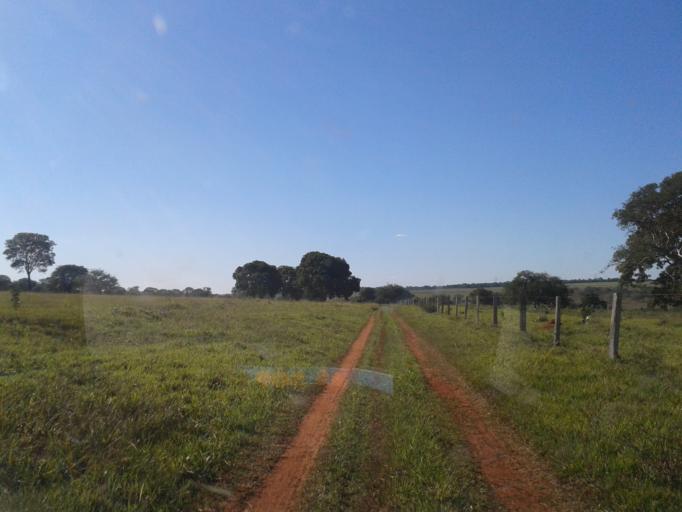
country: BR
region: Minas Gerais
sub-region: Santa Vitoria
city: Santa Vitoria
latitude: -19.0370
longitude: -50.3793
